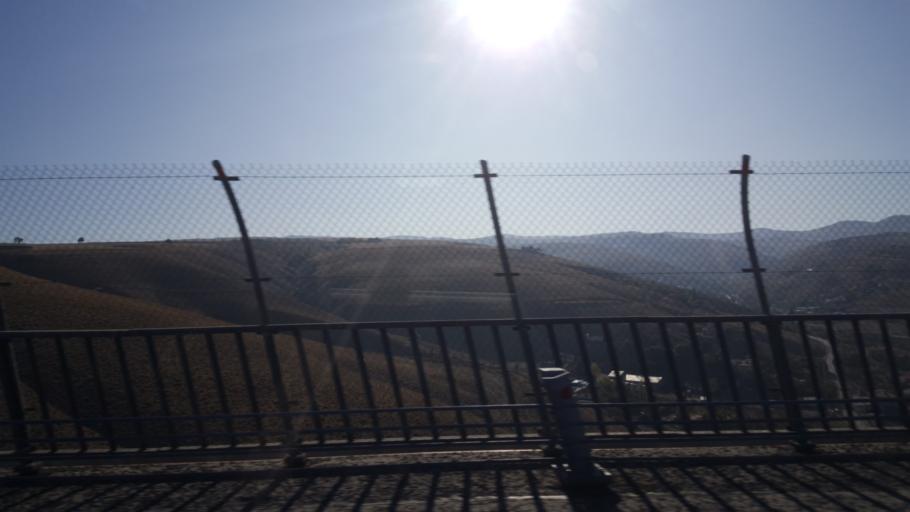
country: TR
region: Ankara
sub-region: Goelbasi
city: Golbasi
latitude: 39.8259
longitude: 32.8808
